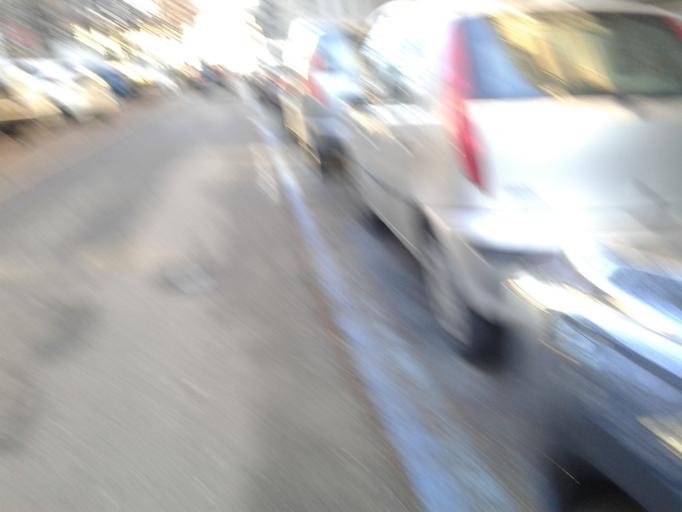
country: IT
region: Piedmont
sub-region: Provincia di Torino
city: Turin
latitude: 45.0564
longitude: 7.6798
